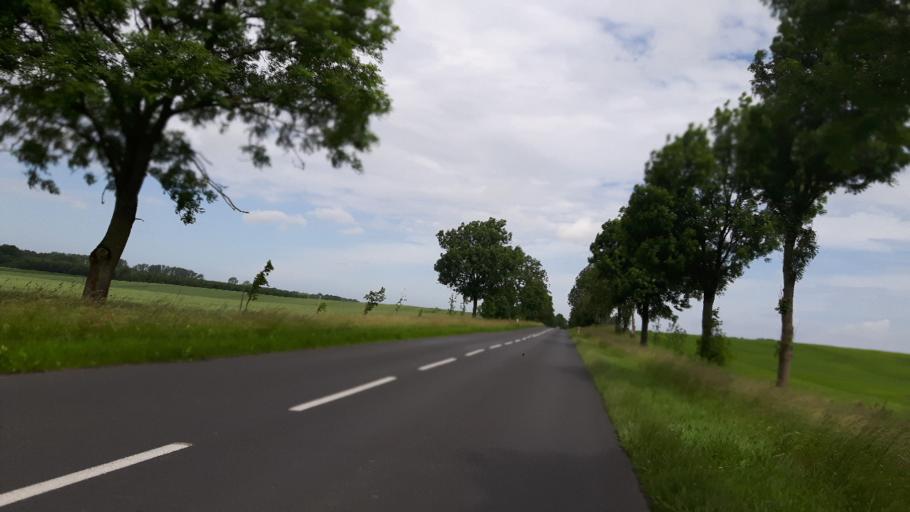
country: PL
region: West Pomeranian Voivodeship
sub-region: Powiat gryficki
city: Trzebiatow
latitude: 54.0240
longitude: 15.2412
